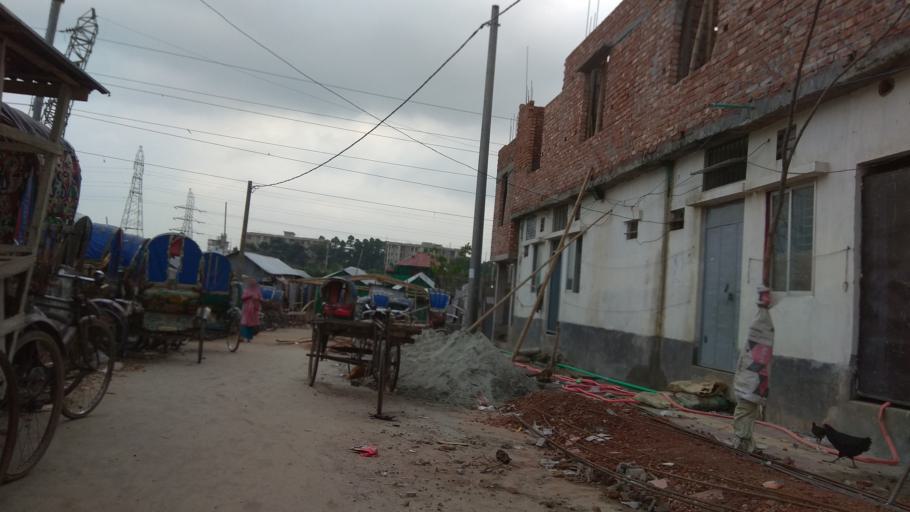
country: BD
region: Dhaka
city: Tungi
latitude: 23.8282
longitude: 90.3569
